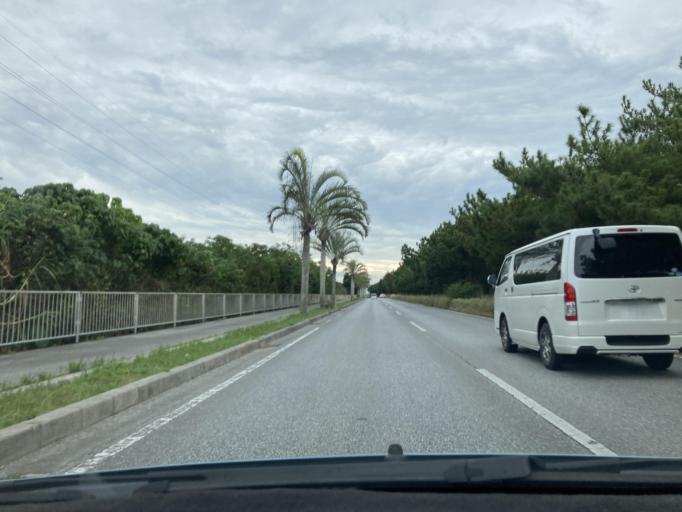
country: JP
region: Okinawa
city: Okinawa
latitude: 26.3904
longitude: 127.7552
